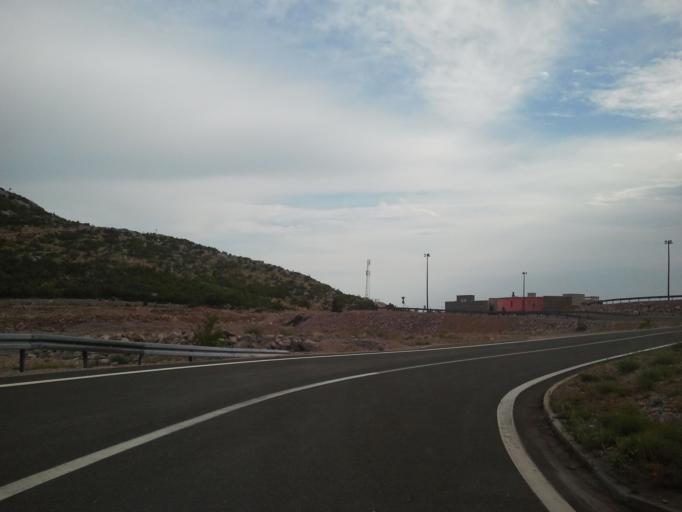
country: HR
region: Zadarska
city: Obrovac
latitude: 44.2513
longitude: 15.6404
